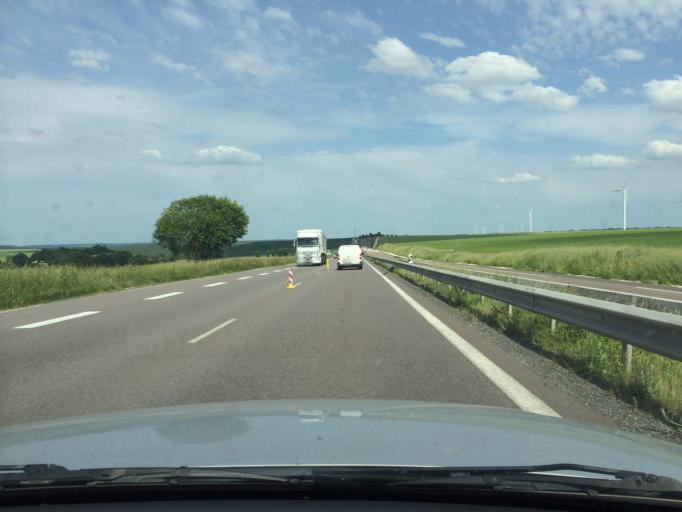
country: FR
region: Lorraine
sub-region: Departement de la Meuse
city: Ligny-en-Barrois
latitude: 48.7023
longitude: 5.4164
